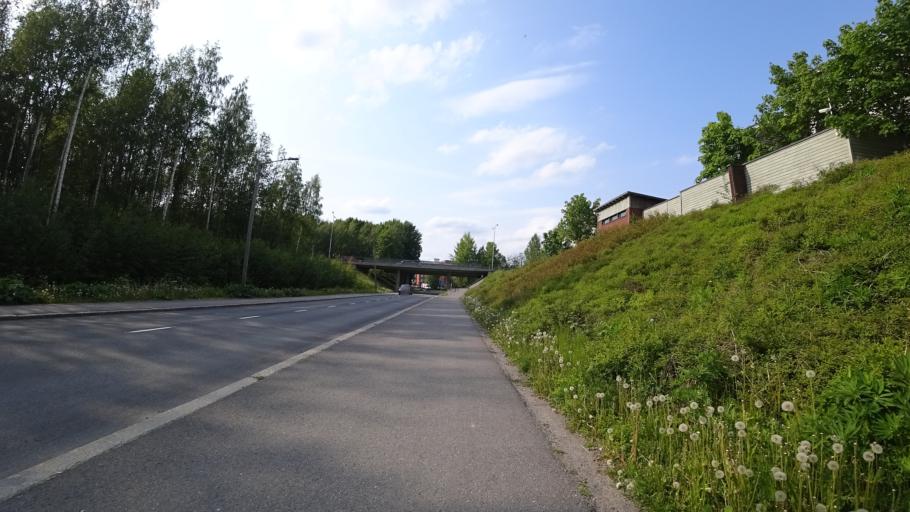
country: FI
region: Pirkanmaa
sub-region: Tampere
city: Pirkkala
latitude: 61.5042
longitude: 23.6834
